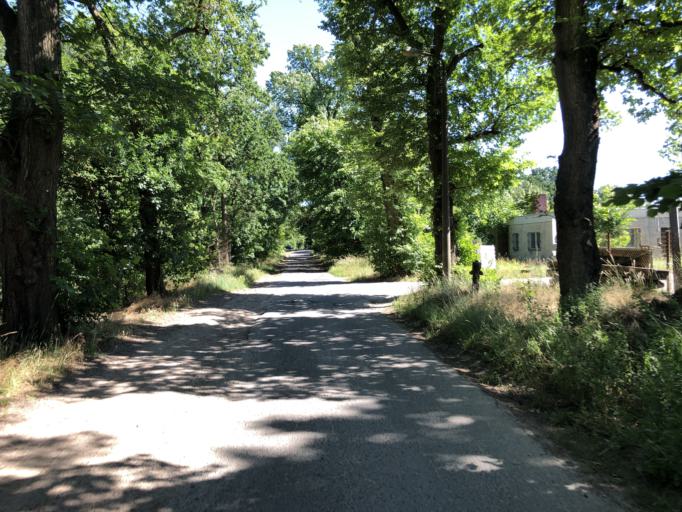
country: DE
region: Berlin
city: Friedrichshagen
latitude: 52.4825
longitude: 13.6349
